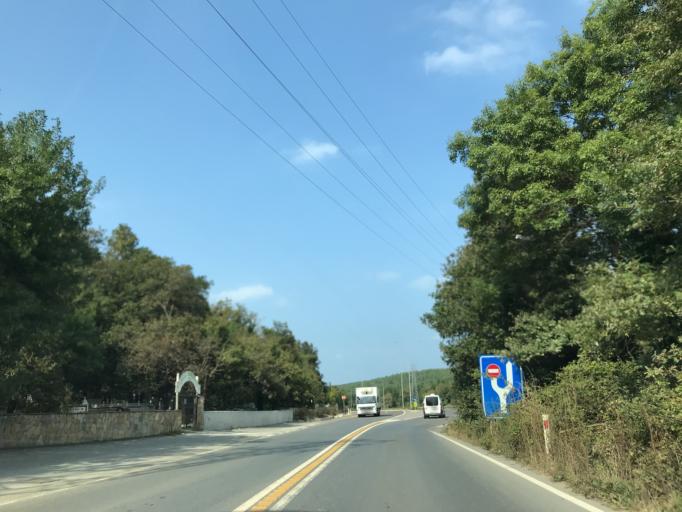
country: TR
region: Istanbul
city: Arikoey
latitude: 41.2339
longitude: 29.0404
